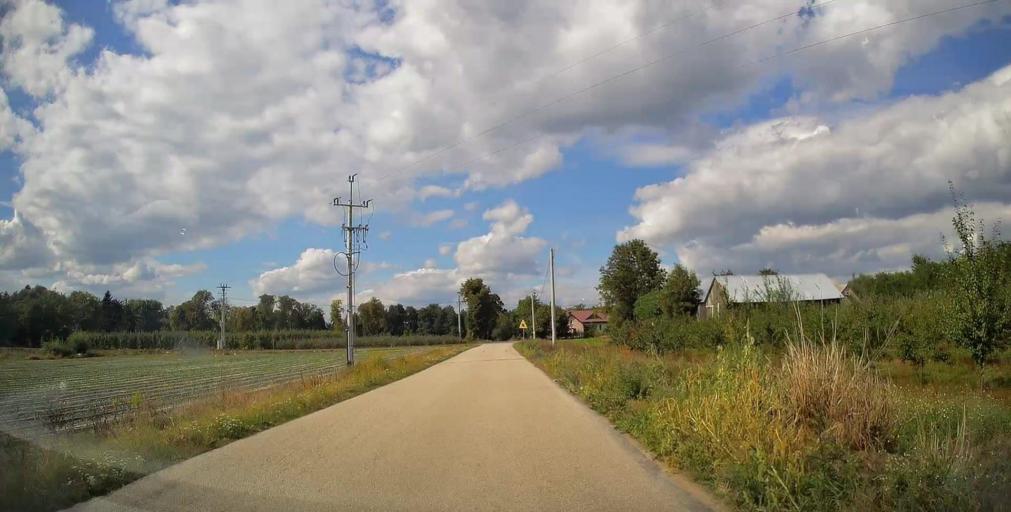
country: PL
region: Masovian Voivodeship
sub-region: Powiat grojecki
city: Goszczyn
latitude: 51.7107
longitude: 20.8890
